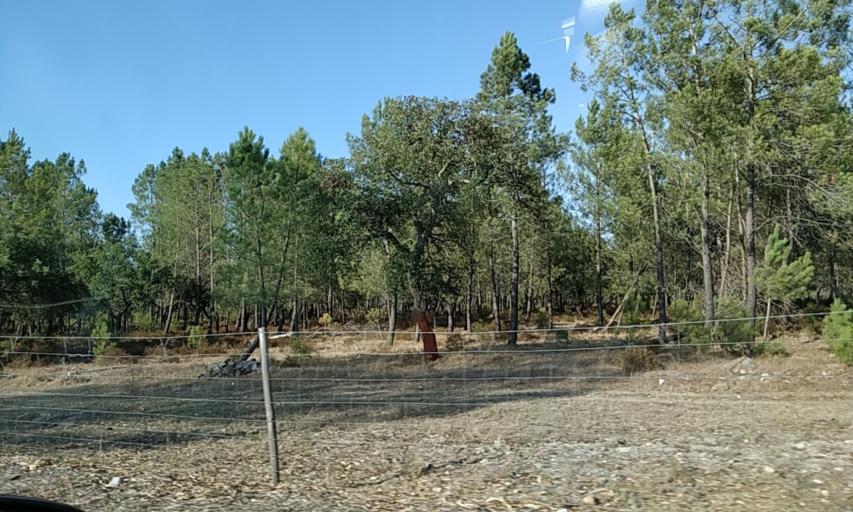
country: PT
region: Santarem
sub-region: Almeirim
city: Fazendas de Almeirim
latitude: 39.1244
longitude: -8.6024
